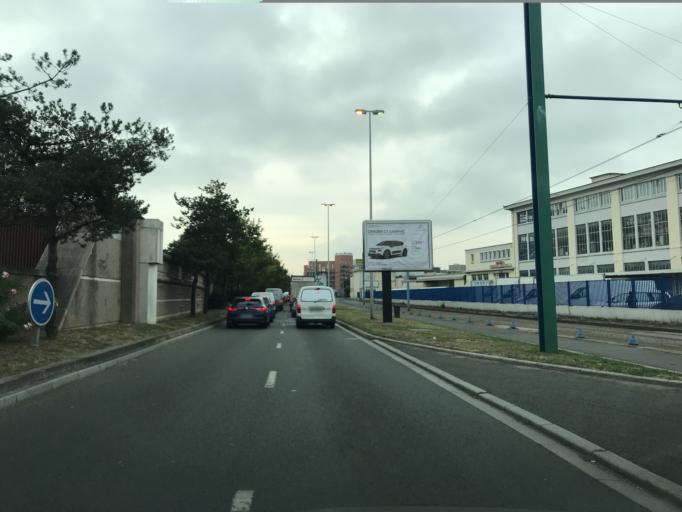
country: FR
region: Ile-de-France
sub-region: Departement de Seine-Saint-Denis
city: Drancy
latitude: 48.9137
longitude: 2.4327
